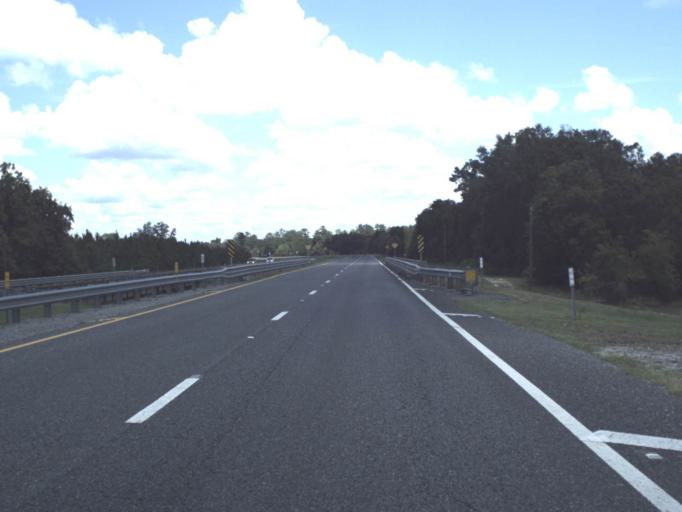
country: US
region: Florida
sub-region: Taylor County
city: Steinhatchee
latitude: 29.7676
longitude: -83.3224
